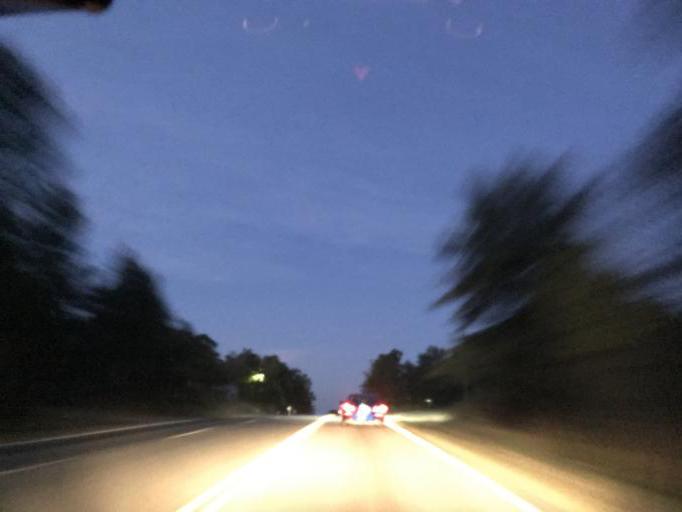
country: US
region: Georgia
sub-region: Jones County
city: Gray
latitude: 32.9007
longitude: -83.5260
